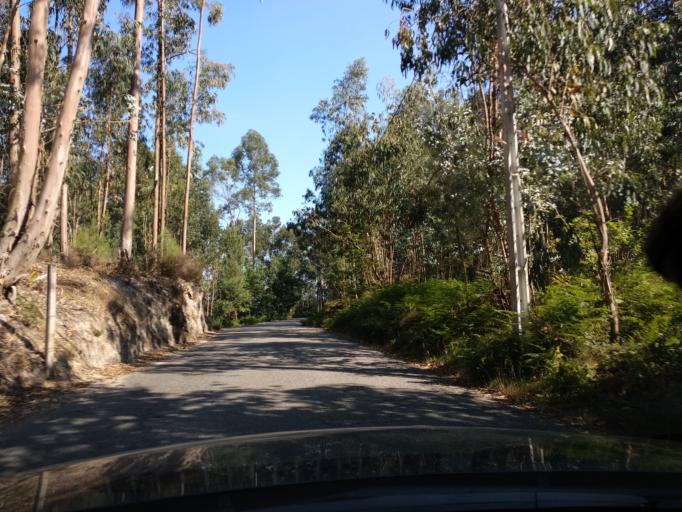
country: PT
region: Porto
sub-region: Paredes
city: Baltar
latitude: 41.2168
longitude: -8.3677
